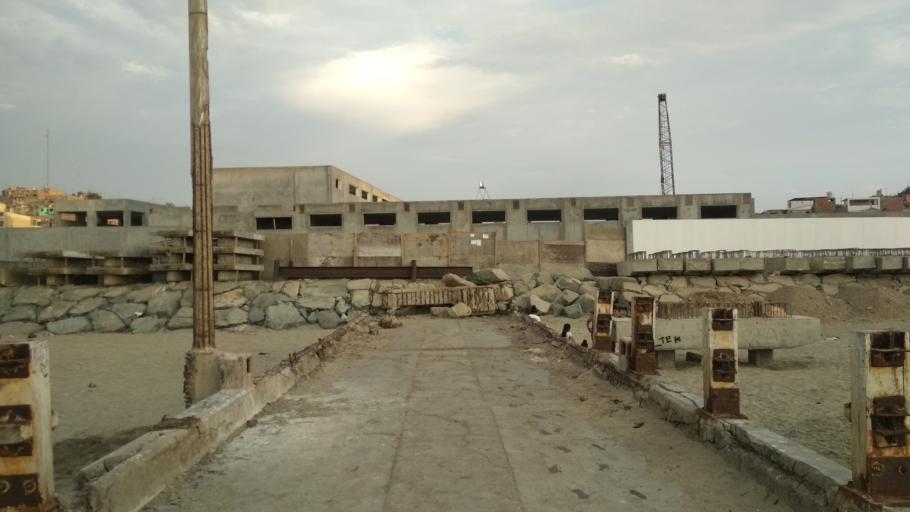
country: PE
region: Lima
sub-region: Barranca
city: Puerto Supe
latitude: -10.8005
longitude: -77.7466
